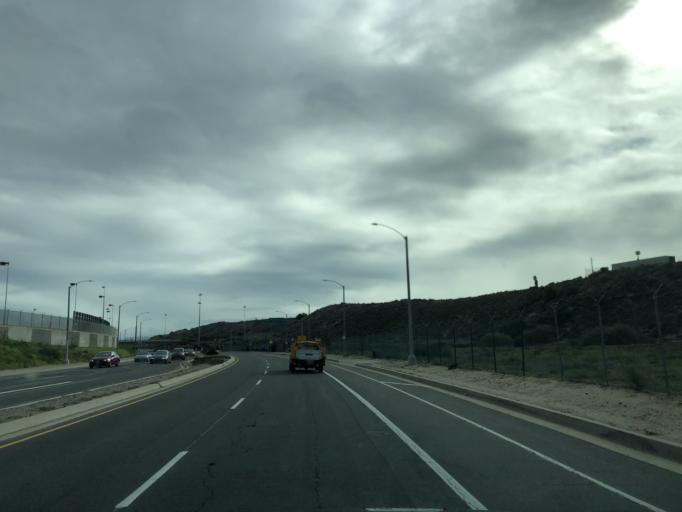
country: US
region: California
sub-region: Los Angeles County
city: El Segundo
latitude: 33.9448
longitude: -118.4364
